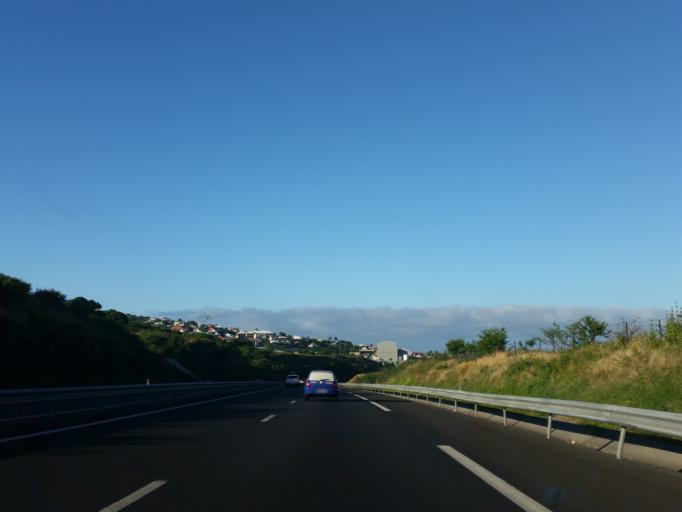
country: RE
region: Reunion
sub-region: Reunion
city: Saint-Leu
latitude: -21.1930
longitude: 55.2962
